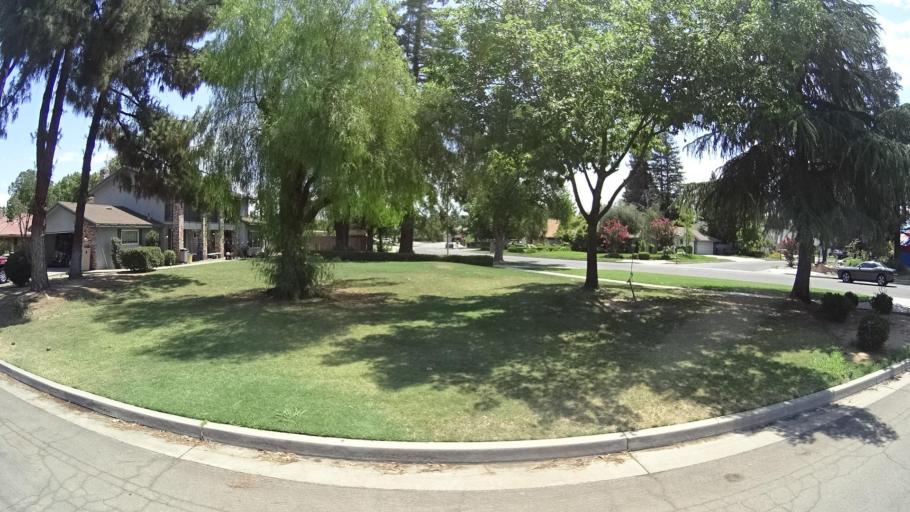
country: US
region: California
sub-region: Fresno County
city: Sunnyside
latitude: 36.7250
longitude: -119.7141
